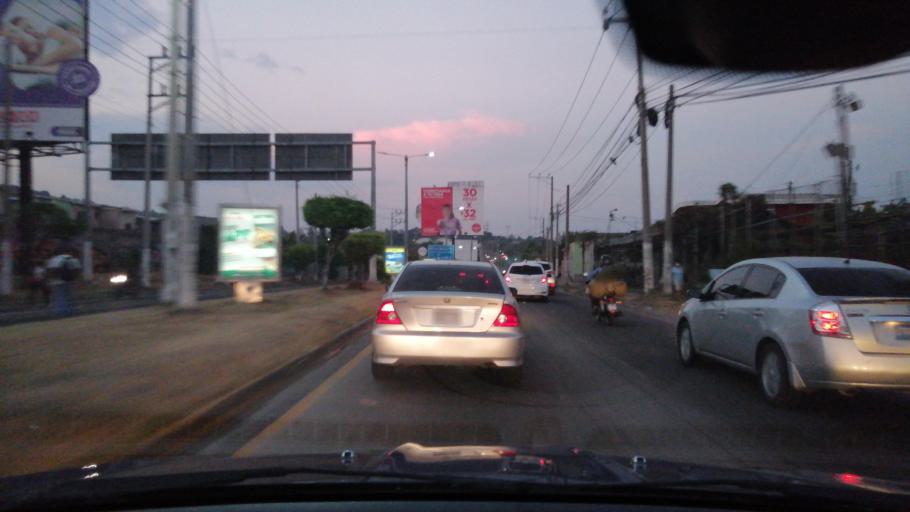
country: SV
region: San Salvador
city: Mejicanos
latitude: 13.7371
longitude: -89.2176
